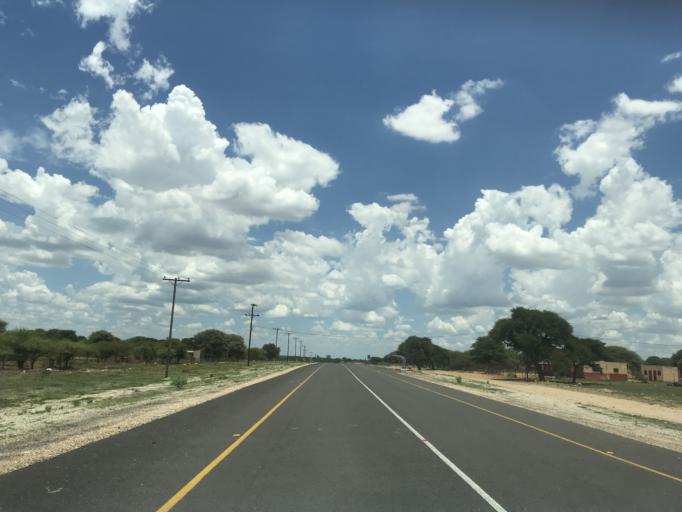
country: BW
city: Mabuli
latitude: -25.7485
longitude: 24.9782
